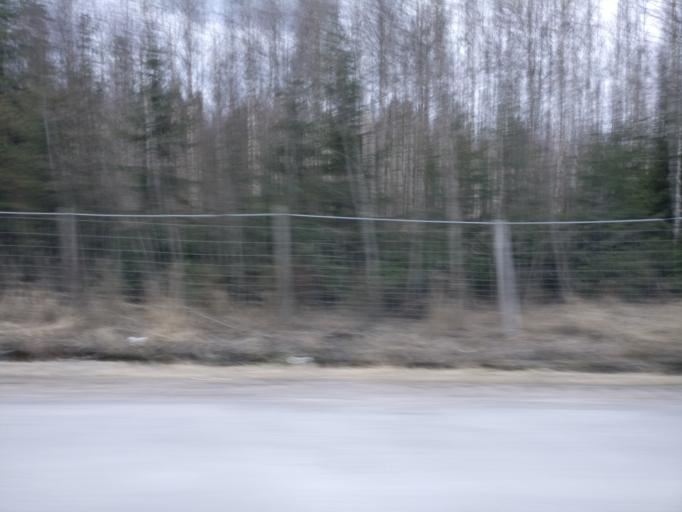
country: FI
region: Uusimaa
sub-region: Helsinki
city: Hyvinge
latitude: 60.6578
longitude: 24.7962
